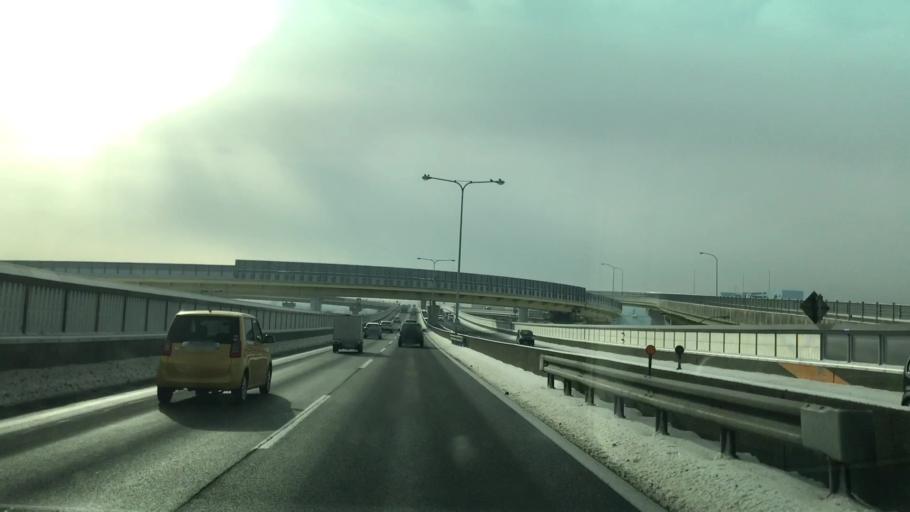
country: JP
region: Hokkaido
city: Sapporo
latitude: 43.0791
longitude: 141.4201
